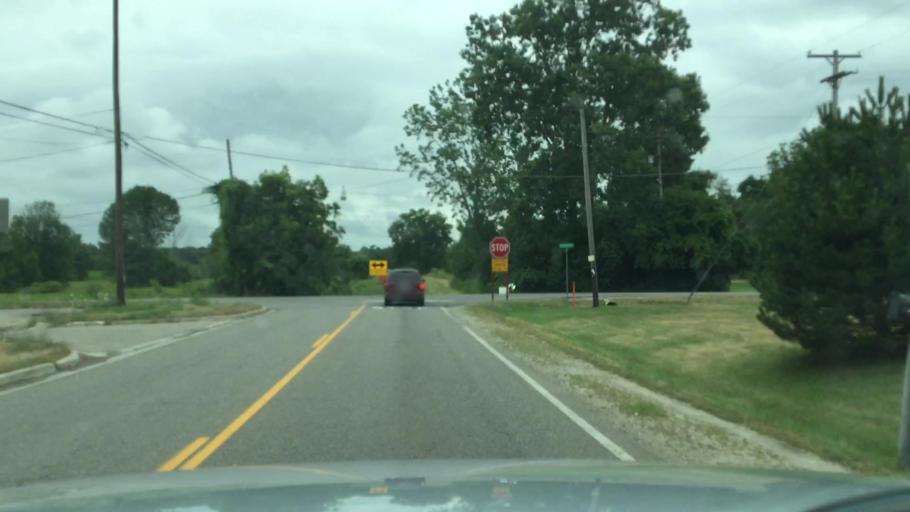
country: US
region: Michigan
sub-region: Genesee County
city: Beecher
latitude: 43.0764
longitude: -83.6371
